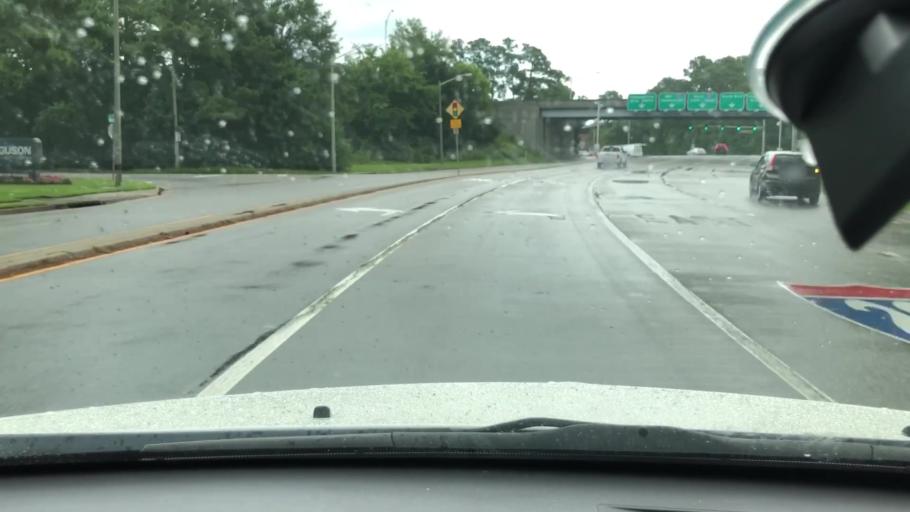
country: US
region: Virginia
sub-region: City of Chesapeake
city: Chesapeake
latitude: 36.8302
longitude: -76.1389
